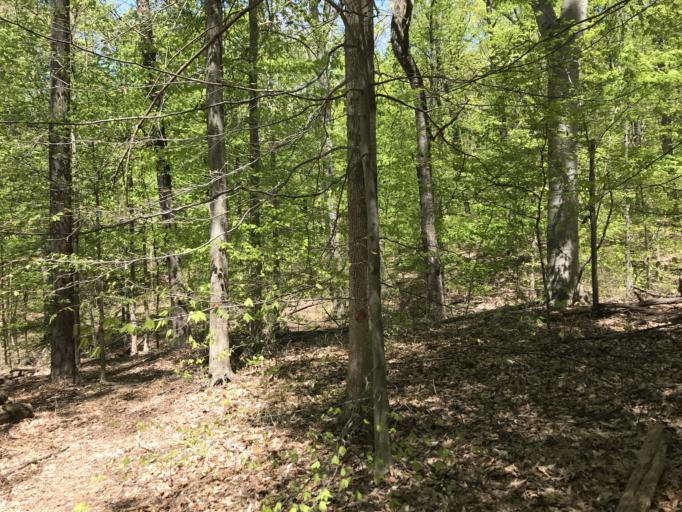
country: US
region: Kentucky
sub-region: Jefferson County
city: Shively
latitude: 38.1567
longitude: -85.7880
